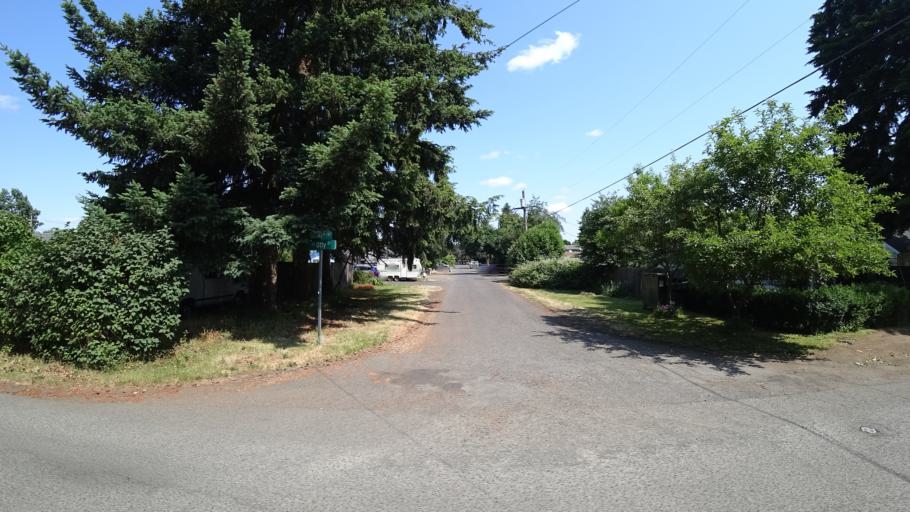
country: US
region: Oregon
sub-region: Multnomah County
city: Lents
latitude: 45.4518
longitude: -122.5846
